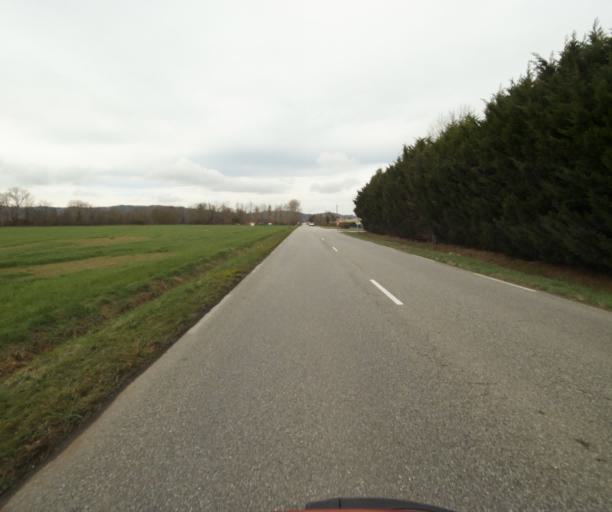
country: FR
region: Midi-Pyrenees
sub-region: Departement de l'Ariege
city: La Tour-du-Crieu
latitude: 43.0993
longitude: 1.6468
